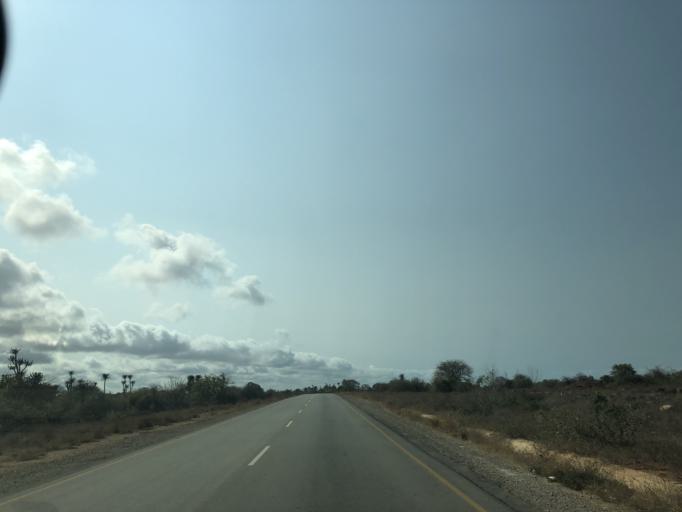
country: AO
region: Luanda
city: Luanda
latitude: -9.7040
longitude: 13.2152
